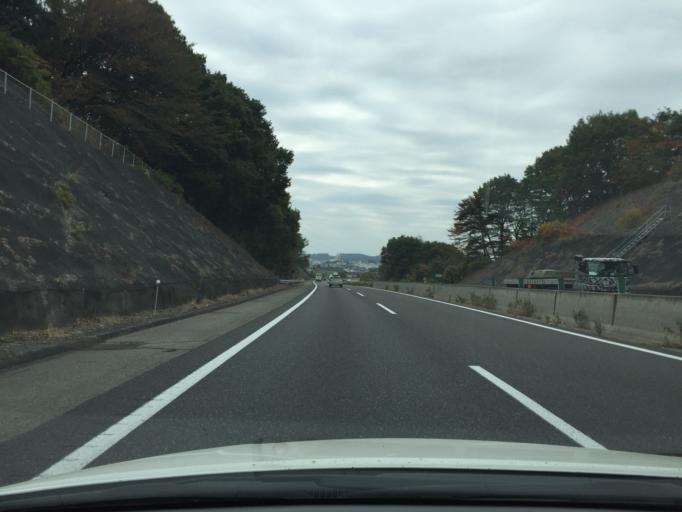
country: JP
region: Fukushima
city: Sukagawa
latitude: 37.1450
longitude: 140.2007
